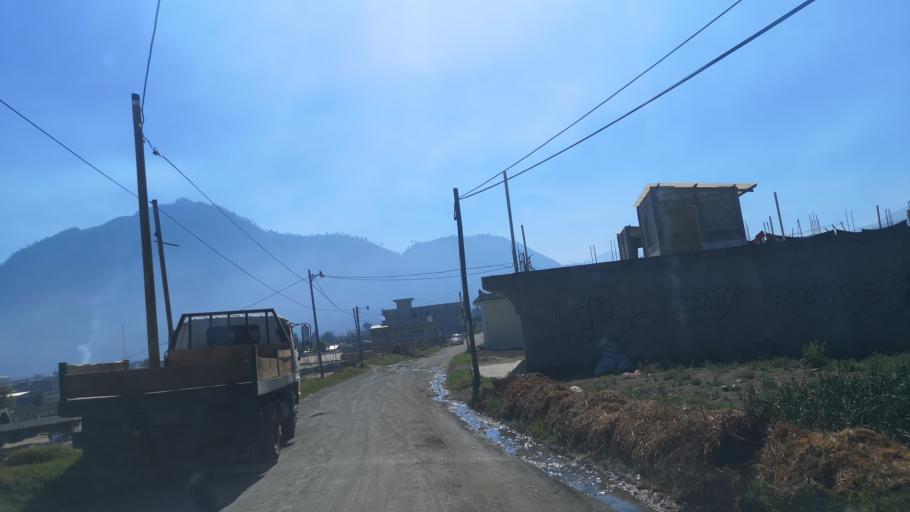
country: GT
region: Quetzaltenango
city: Quetzaltenango
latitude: 14.7934
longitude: -91.5513
